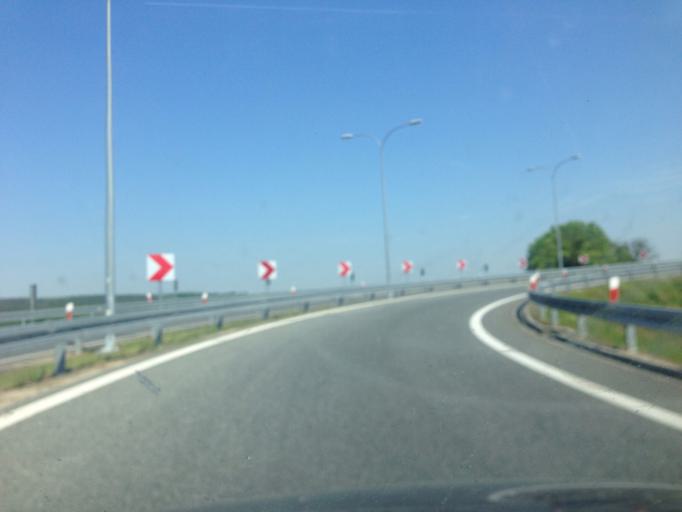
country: PL
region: Pomeranian Voivodeship
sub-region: Powiat tczewski
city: Pelplin
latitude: 53.9324
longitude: 18.6391
